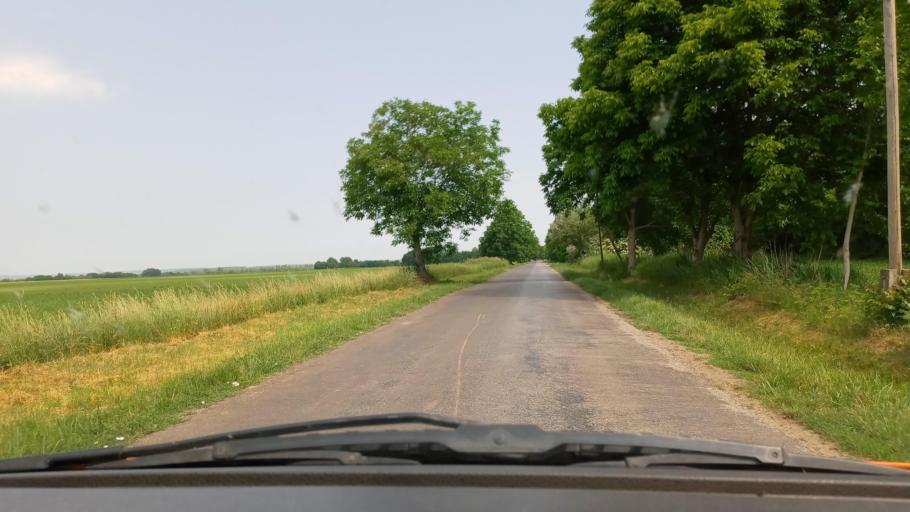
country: HU
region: Baranya
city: Szentlorinc
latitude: 45.9964
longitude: 18.0367
